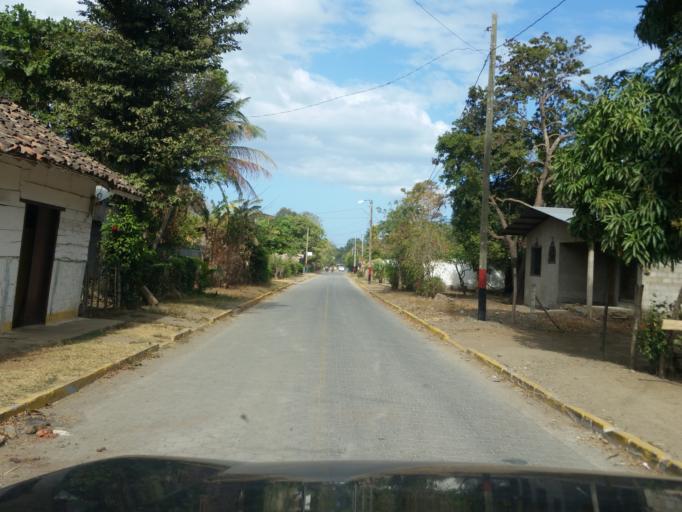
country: NI
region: Rivas
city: Potosi
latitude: 11.4918
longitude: -85.8587
